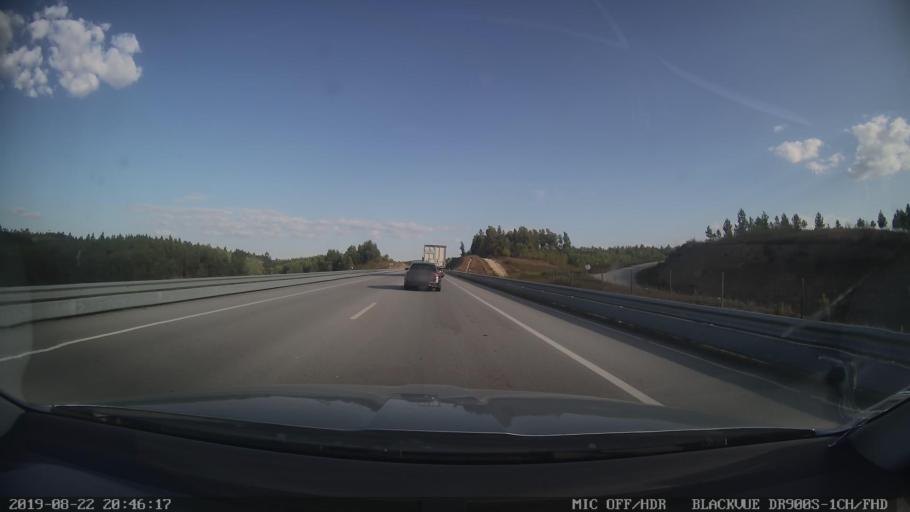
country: PT
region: Castelo Branco
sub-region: Proenca-A-Nova
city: Proenca-a-Nova
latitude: 39.7252
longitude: -7.8750
